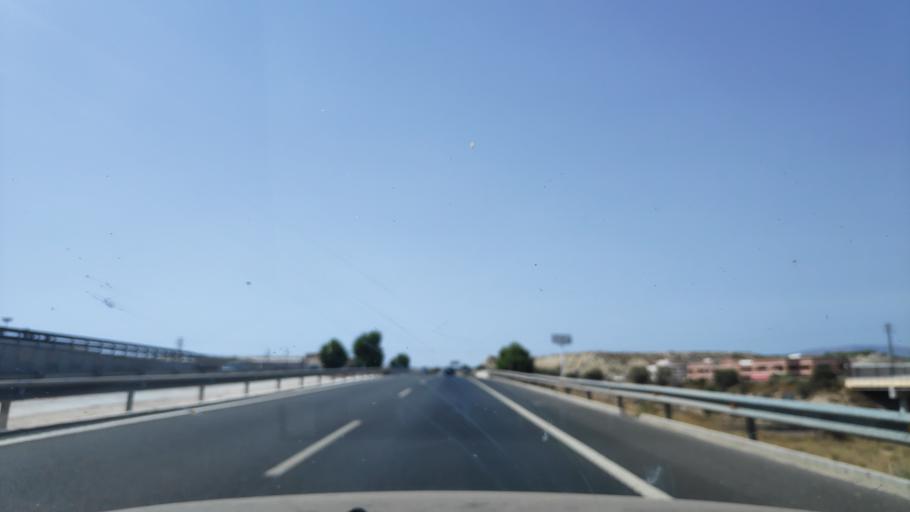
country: ES
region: Murcia
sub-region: Murcia
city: Lorqui
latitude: 38.1015
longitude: -1.2330
